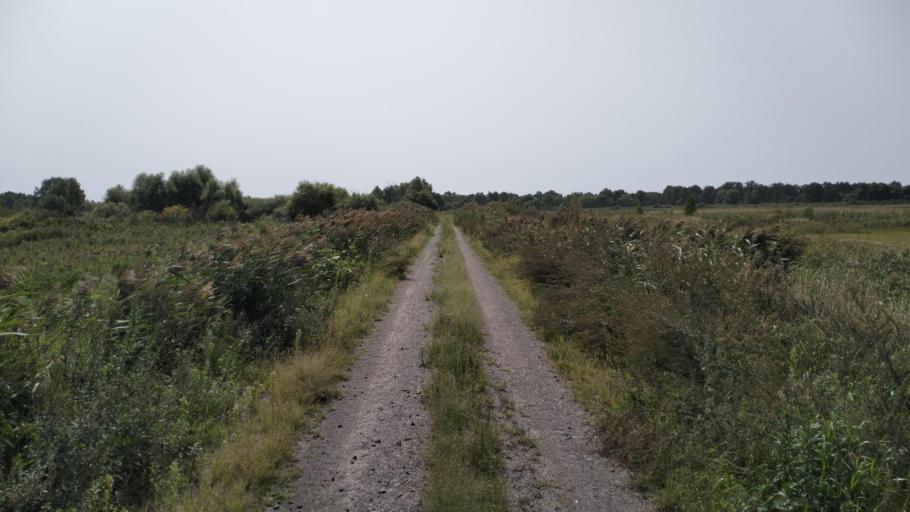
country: BY
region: Brest
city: Davyd-Haradok
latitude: 51.9692
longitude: 27.1736
